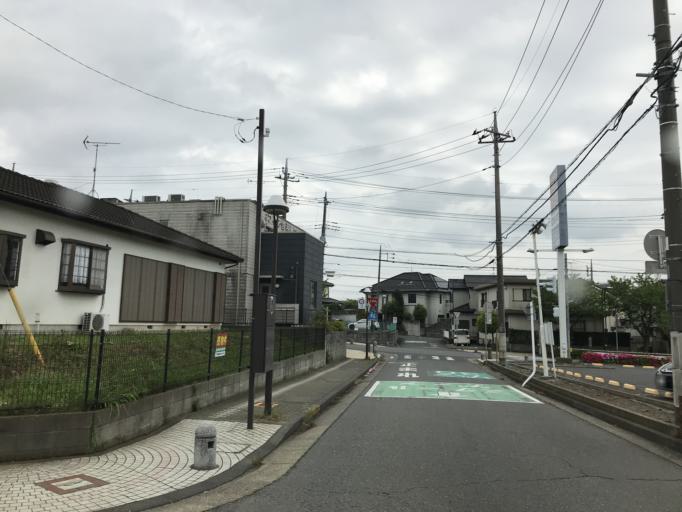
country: JP
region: Ibaraki
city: Mitsukaido
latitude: 35.9801
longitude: 139.9807
